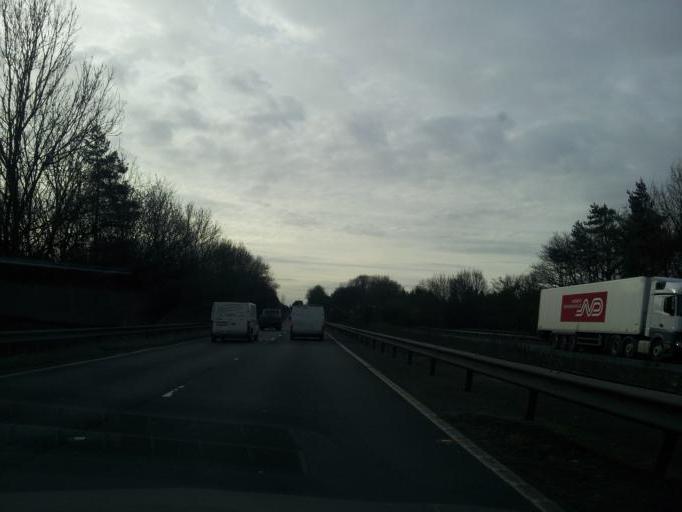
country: GB
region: England
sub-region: District of Rutland
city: Greetham
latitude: 52.7349
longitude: -0.6002
